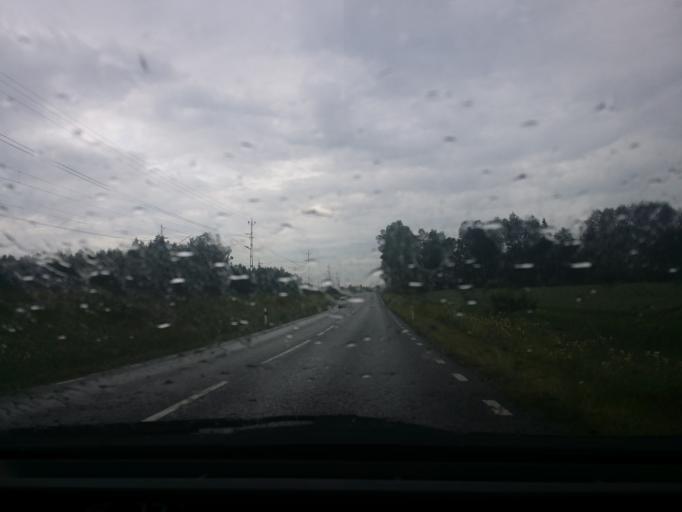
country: SE
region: OErebro
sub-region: Lindesbergs Kommun
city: Frovi
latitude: 59.4634
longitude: 15.3242
